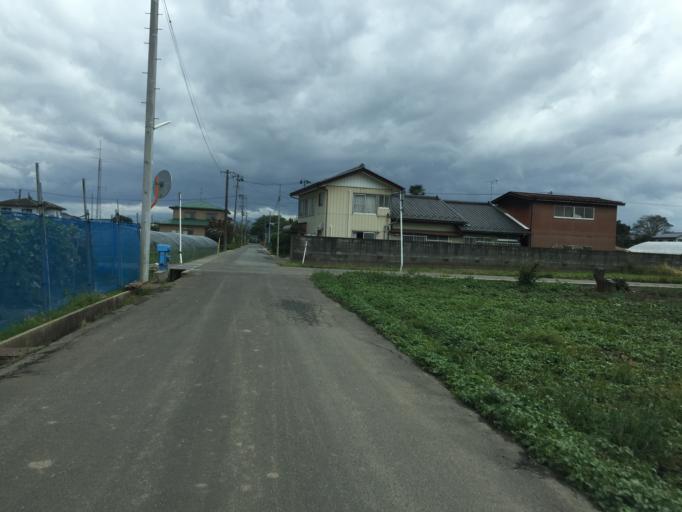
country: JP
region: Fukushima
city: Hobaramachi
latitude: 37.8303
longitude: 140.5469
